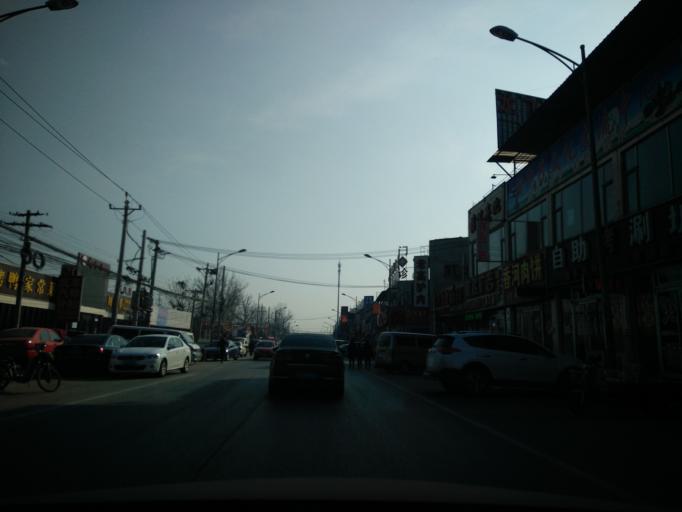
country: CN
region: Beijing
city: Jiugong
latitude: 39.8277
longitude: 116.4990
